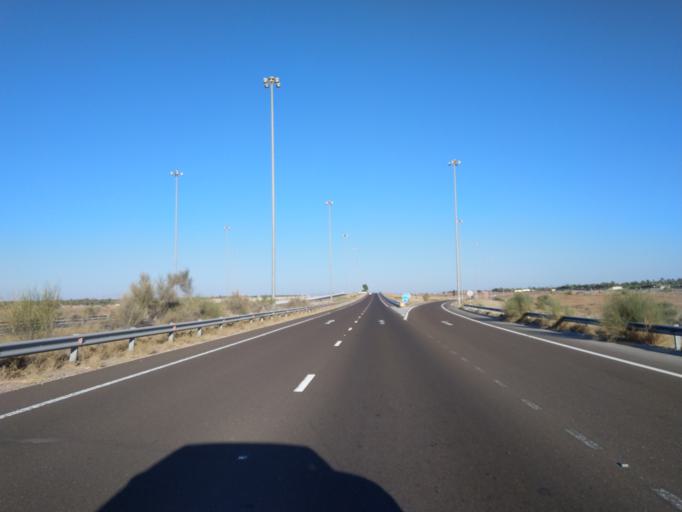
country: OM
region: Al Buraimi
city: Al Buraymi
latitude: 24.5378
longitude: 55.5983
